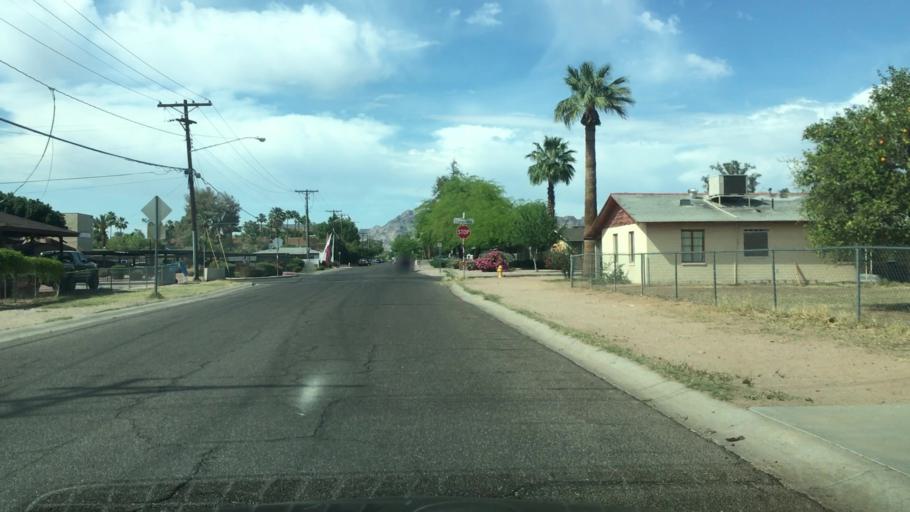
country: US
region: Arizona
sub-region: Maricopa County
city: Phoenix
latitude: 33.4908
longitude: -112.0237
